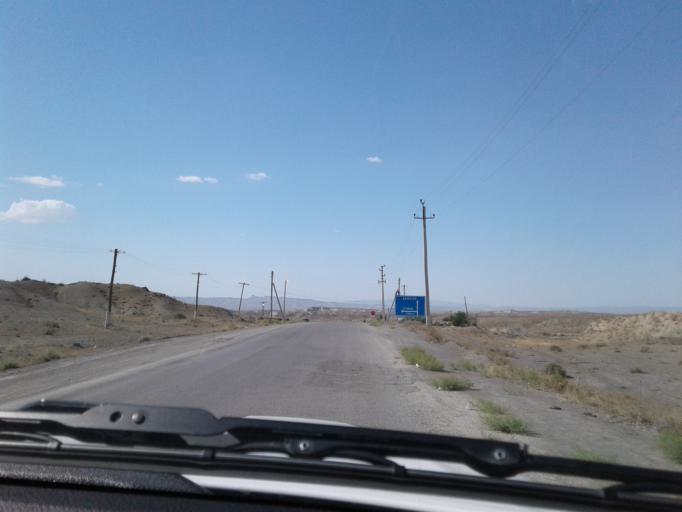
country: TM
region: Balkan
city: Magtymguly
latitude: 38.5007
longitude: 56.1929
